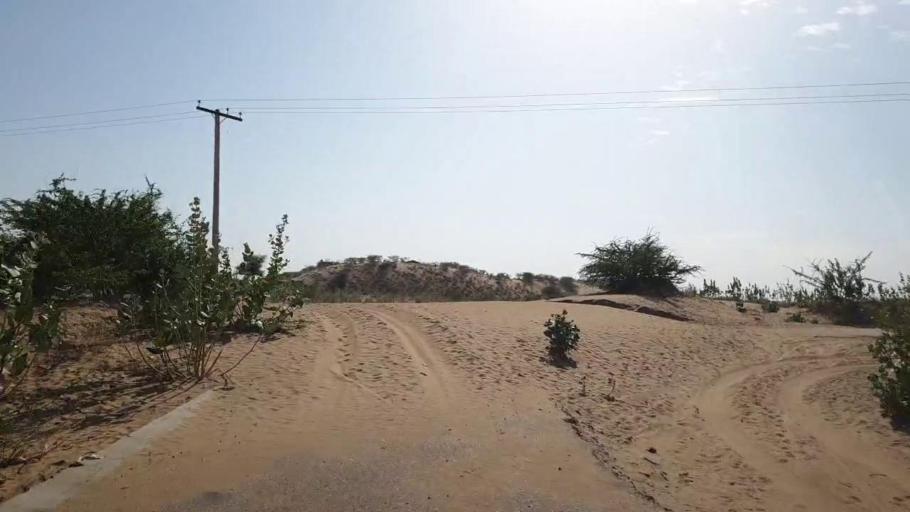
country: PK
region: Sindh
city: Nabisar
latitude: 25.0425
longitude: 70.0169
